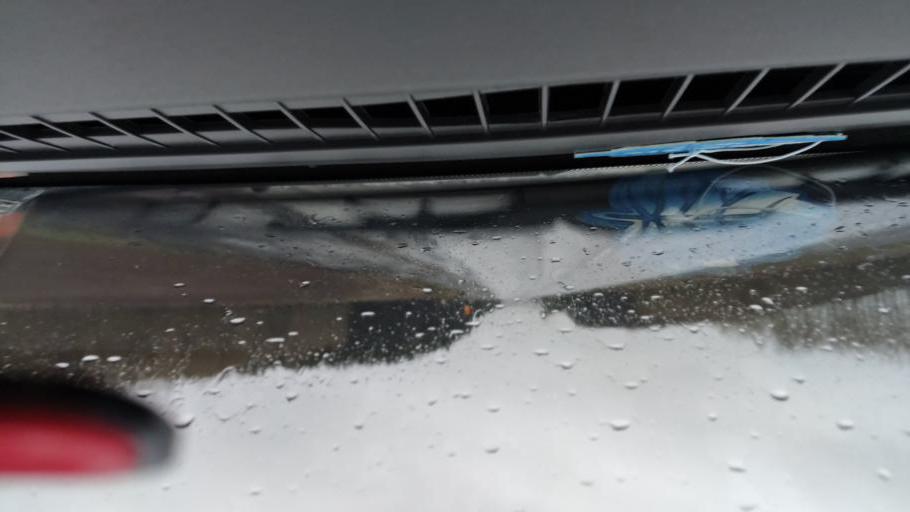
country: RU
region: Tatarstan
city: Mendeleyevsk
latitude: 55.9471
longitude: 52.2983
